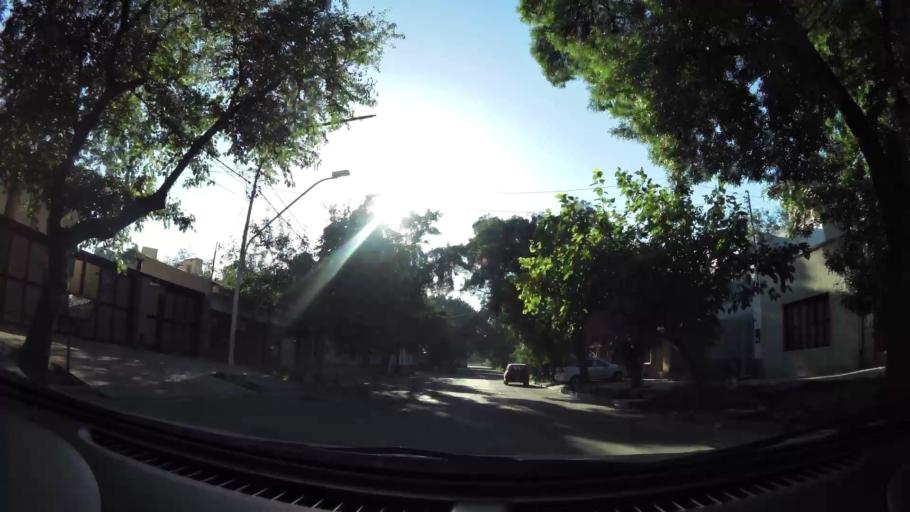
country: AR
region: Mendoza
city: Mendoza
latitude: -32.8735
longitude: -68.8227
